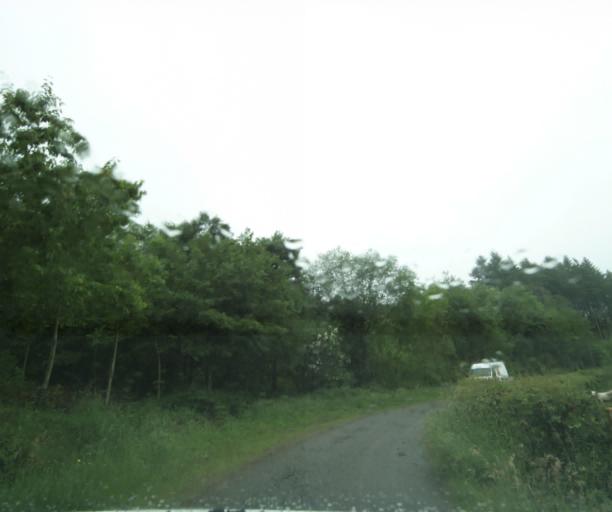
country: FR
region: Bourgogne
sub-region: Departement de Saone-et-Loire
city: Charolles
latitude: 46.3780
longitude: 4.3581
